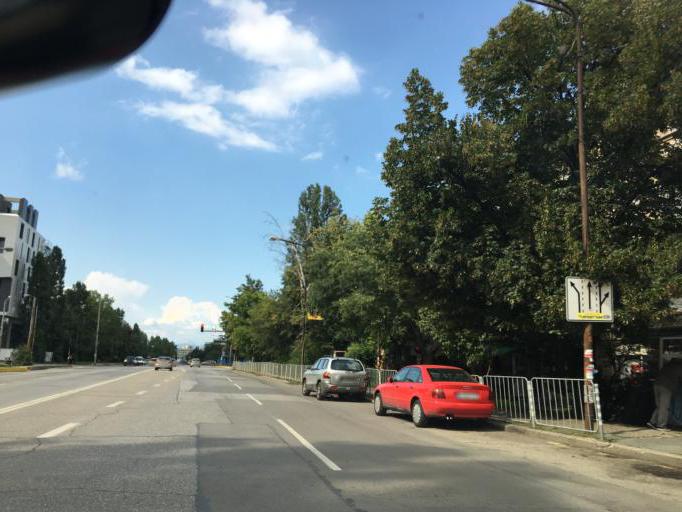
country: BG
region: Sofia-Capital
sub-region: Stolichna Obshtina
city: Sofia
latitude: 42.6564
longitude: 23.3592
